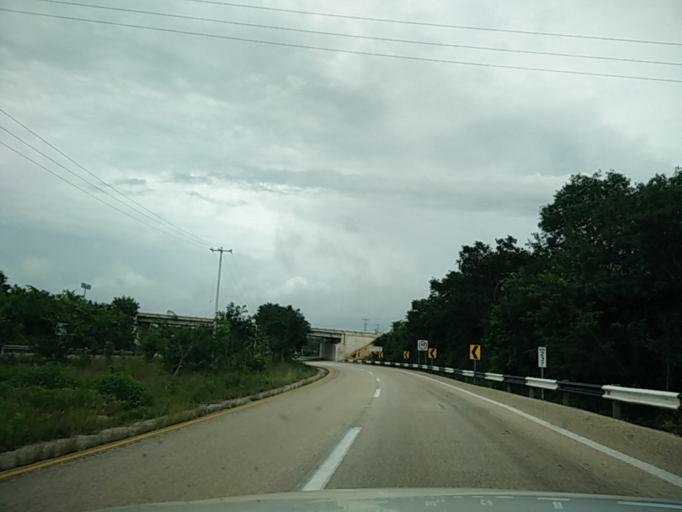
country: MX
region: Quintana Roo
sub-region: Lazaro Cardenas
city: El Tintal
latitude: 20.8981
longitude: -87.4426
